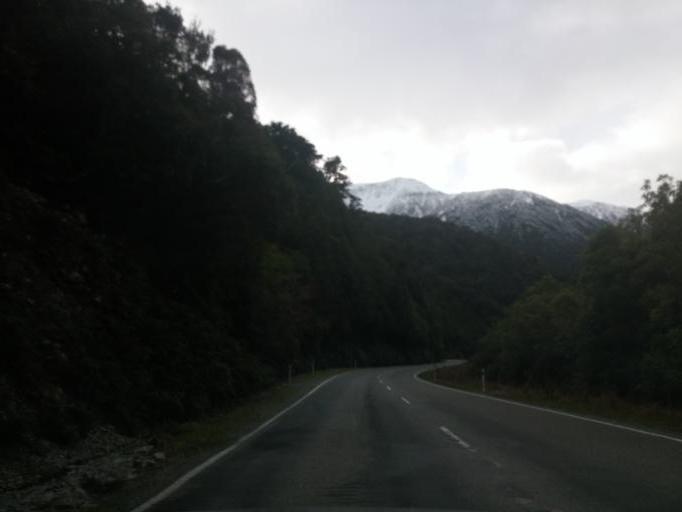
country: NZ
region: West Coast
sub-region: Grey District
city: Greymouth
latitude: -42.8143
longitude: 171.5653
